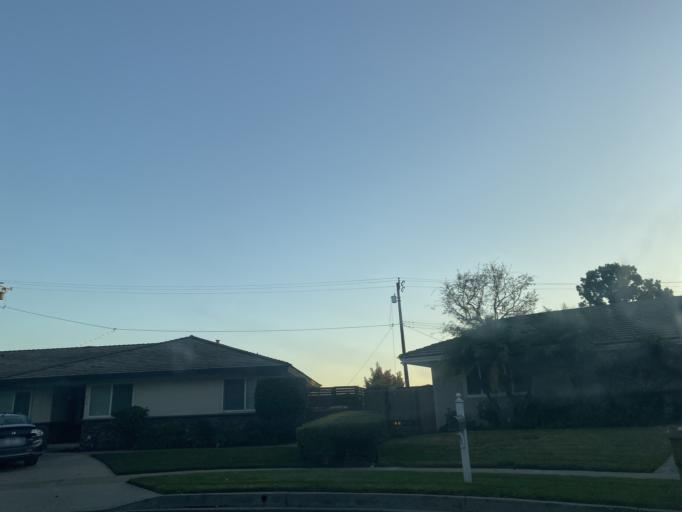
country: US
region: California
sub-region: Orange County
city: Fullerton
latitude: 33.8817
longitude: -117.9149
